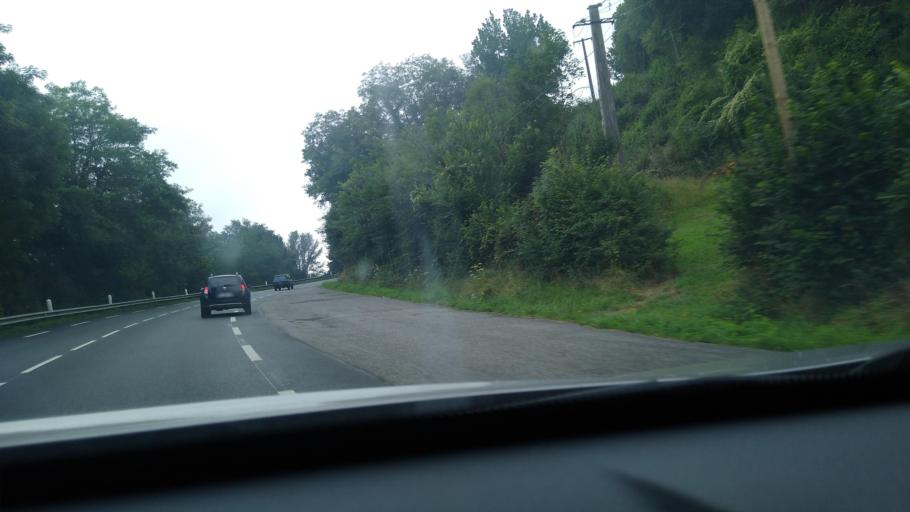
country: FR
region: Midi-Pyrenees
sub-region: Departement de la Haute-Garonne
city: Salies-du-Salat
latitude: 43.0725
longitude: 0.9652
